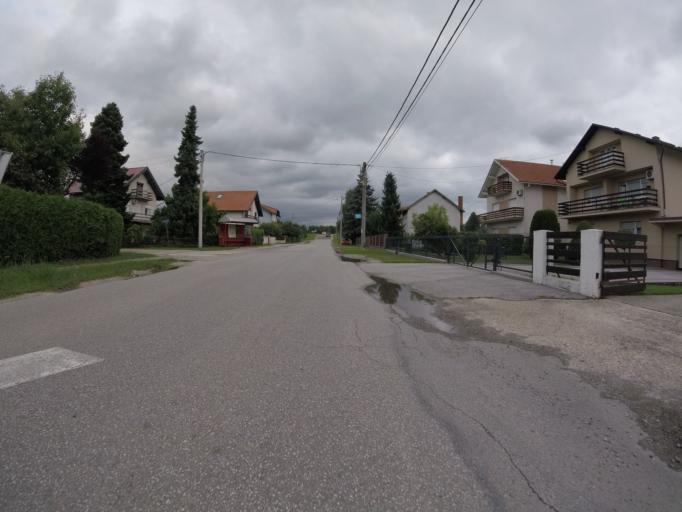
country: HR
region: Zagrebacka
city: Gradici
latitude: 45.7010
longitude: 16.0372
